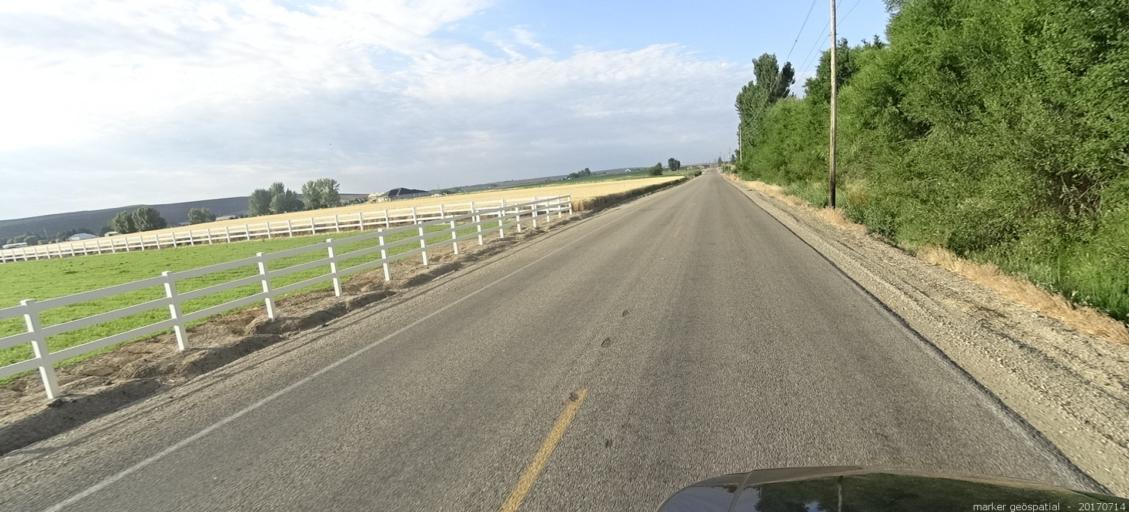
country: US
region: Idaho
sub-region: Ada County
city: Kuna
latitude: 43.4590
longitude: -116.4937
